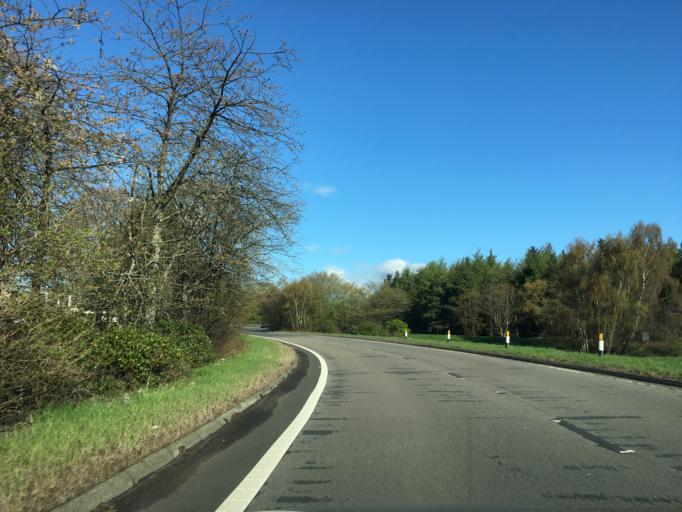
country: GB
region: Scotland
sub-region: Stirling
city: Bridge of Allan
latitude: 56.1323
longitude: -3.9713
